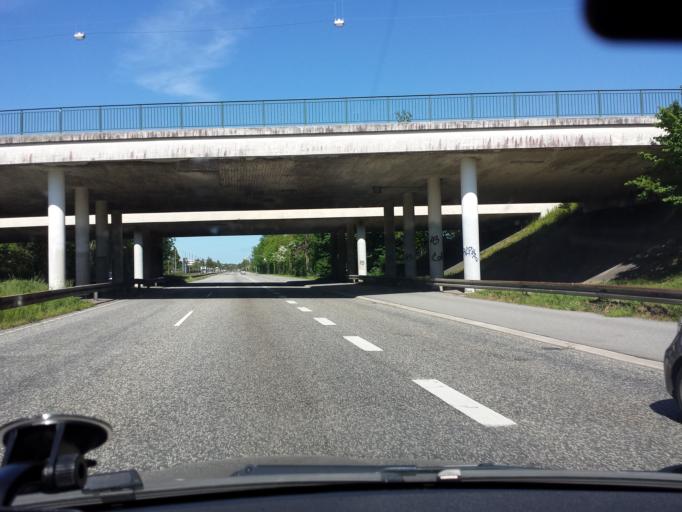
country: DK
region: Capital Region
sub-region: Herlev Kommune
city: Herlev
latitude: 55.7054
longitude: 12.4267
